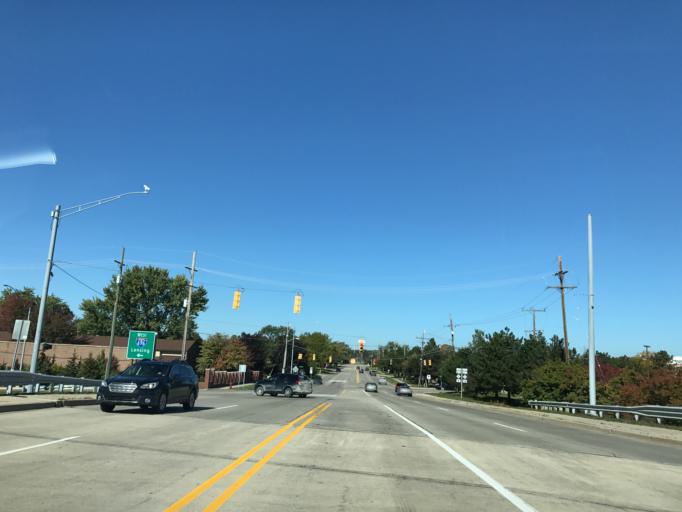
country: US
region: Michigan
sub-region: Oakland County
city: Franklin
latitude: 42.4937
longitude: -83.3000
